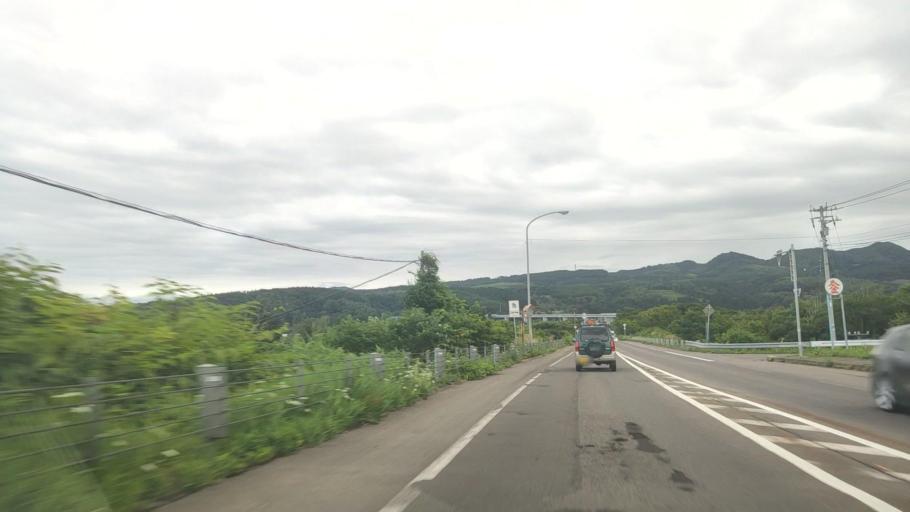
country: JP
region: Hokkaido
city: Nanae
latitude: 42.1965
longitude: 140.4199
